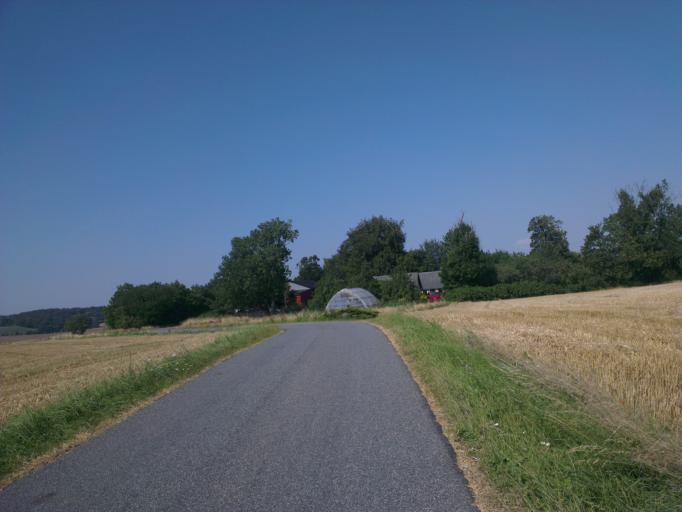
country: DK
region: Capital Region
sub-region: Frederikssund Kommune
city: Skibby
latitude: 55.7514
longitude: 11.9495
